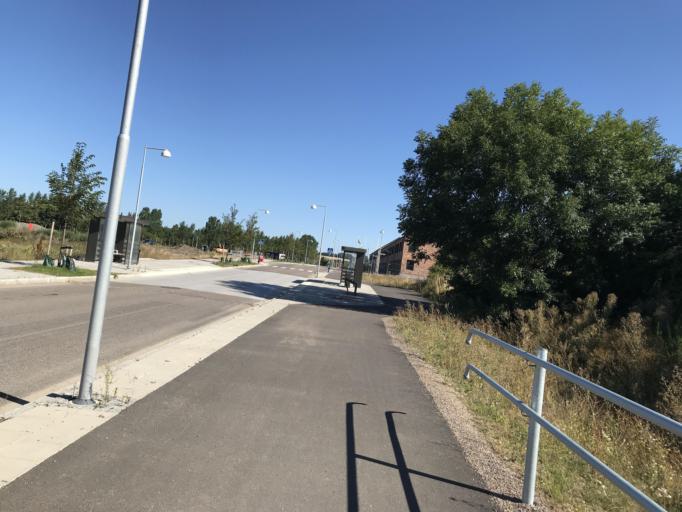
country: SE
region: Skane
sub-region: Landskrona
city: Landskrona
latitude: 55.9013
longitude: 12.8140
